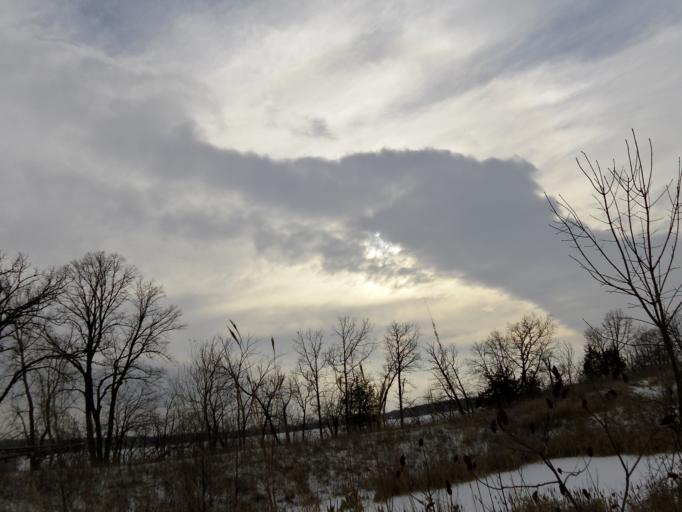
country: US
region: Minnesota
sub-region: Scott County
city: Prior Lake
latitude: 44.7069
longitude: -93.4708
